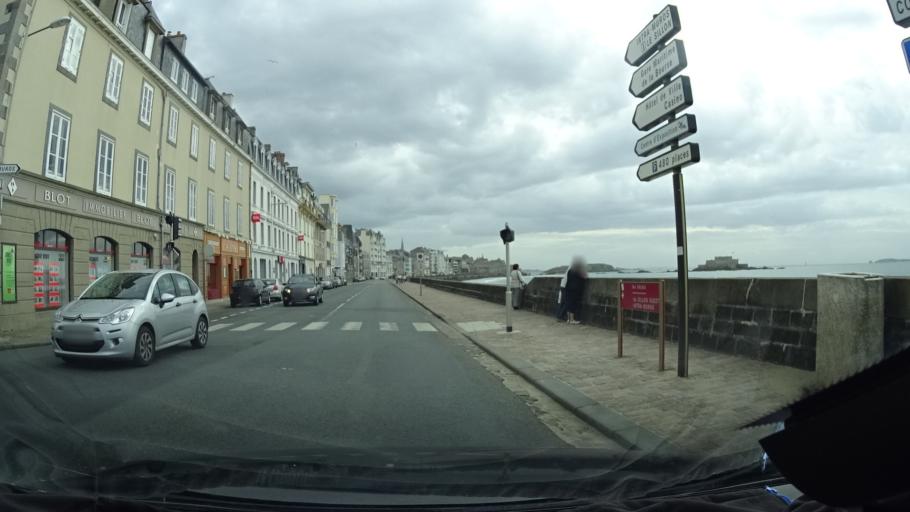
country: FR
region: Brittany
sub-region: Departement d'Ille-et-Vilaine
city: Saint-Malo
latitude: 48.6535
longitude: -2.0115
